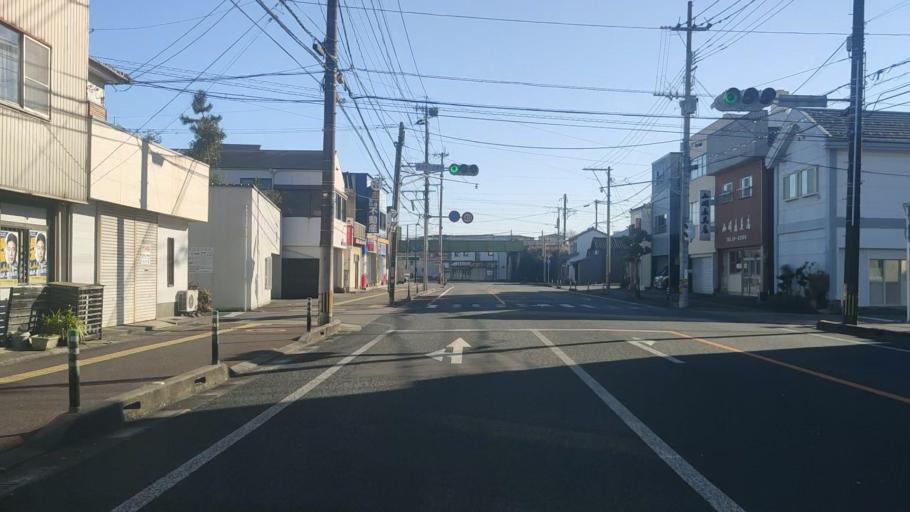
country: JP
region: Miyazaki
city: Nobeoka
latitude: 32.5854
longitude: 131.6721
